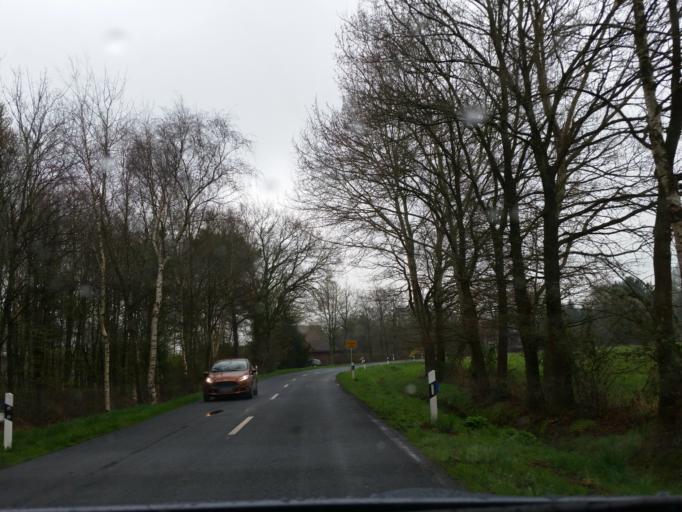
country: DE
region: Lower Saxony
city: Hipstedt
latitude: 53.4846
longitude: 8.9586
